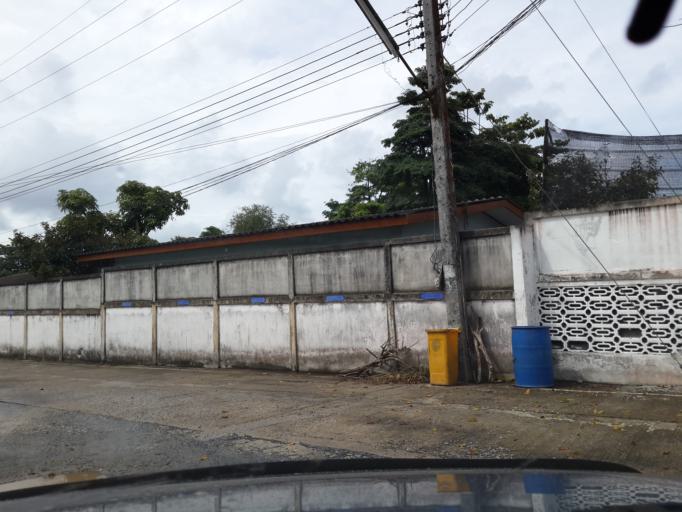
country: TH
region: Narathiwat
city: Rueso
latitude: 6.3865
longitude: 101.5150
